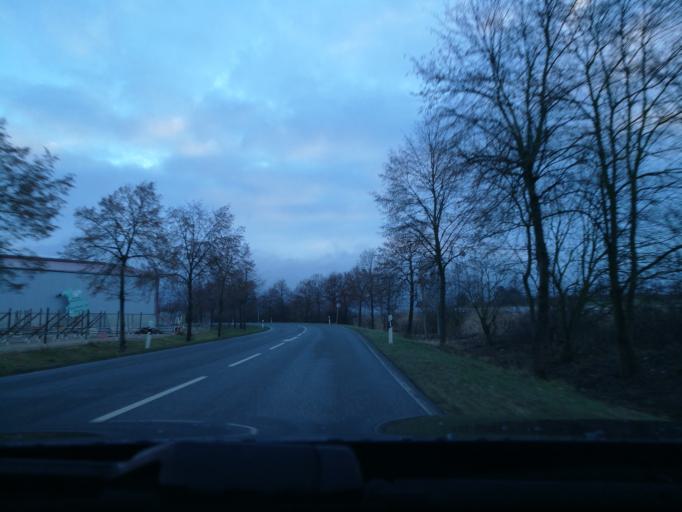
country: DE
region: Bavaria
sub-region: Regierungsbezirk Mittelfranken
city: Baiersdorf
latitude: 49.6486
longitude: 11.0275
